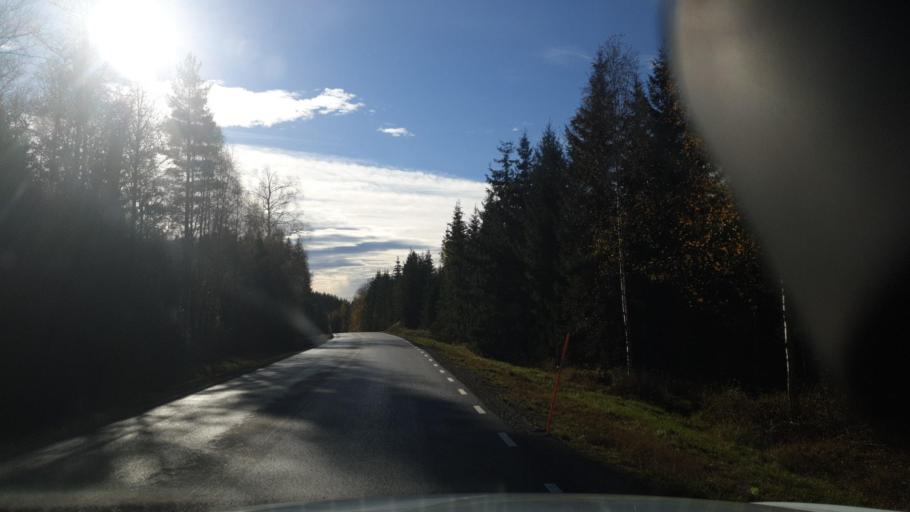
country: SE
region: Vaermland
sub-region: Arvika Kommun
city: Arvika
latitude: 59.9301
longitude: 12.6629
